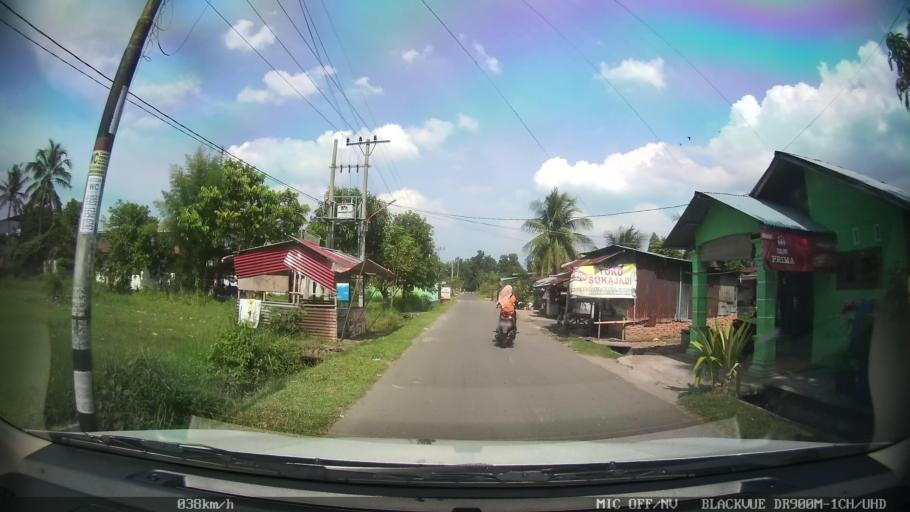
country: ID
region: North Sumatra
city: Binjai
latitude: 3.6133
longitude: 98.5324
